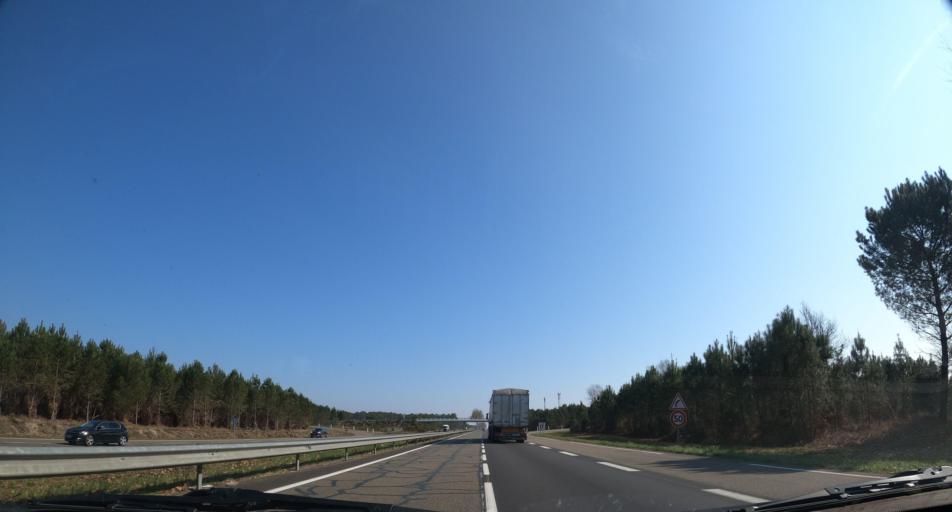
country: FR
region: Aquitaine
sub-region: Departement des Landes
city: Riviere-Saas-et-Gourby
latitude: 43.7073
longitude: -1.1657
